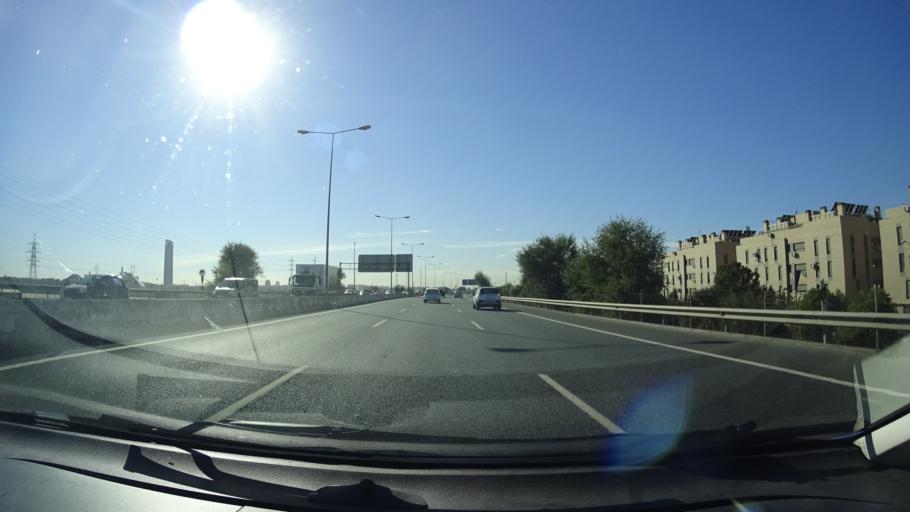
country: ES
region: Andalusia
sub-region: Provincia de Sevilla
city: Camas
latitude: 37.4001
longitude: -6.0271
